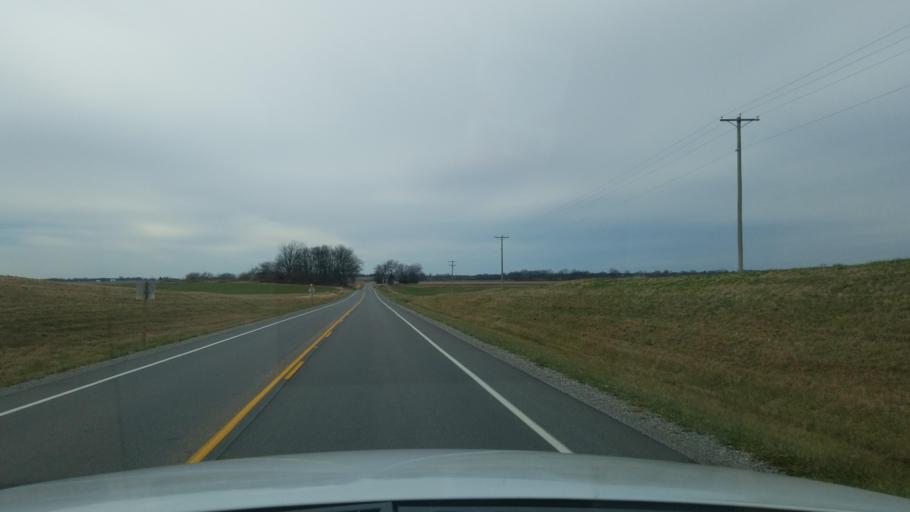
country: US
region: Illinois
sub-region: White County
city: Carmi
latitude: 37.9076
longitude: -88.1559
